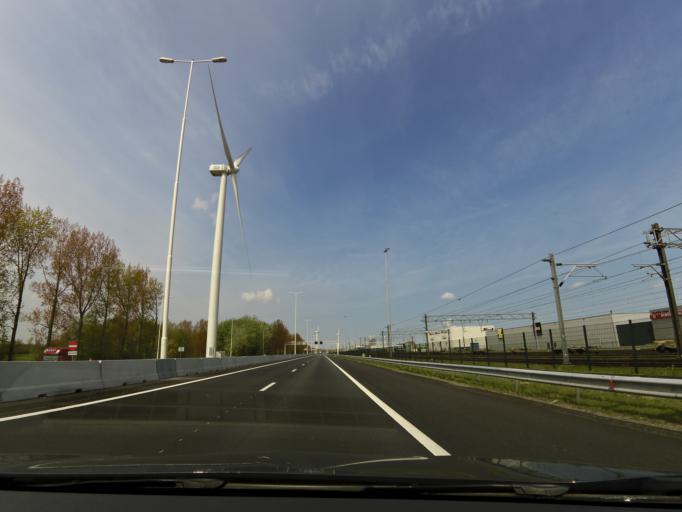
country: NL
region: South Holland
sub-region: Gemeente Brielle
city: Brielle
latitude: 51.9140
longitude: 4.1898
